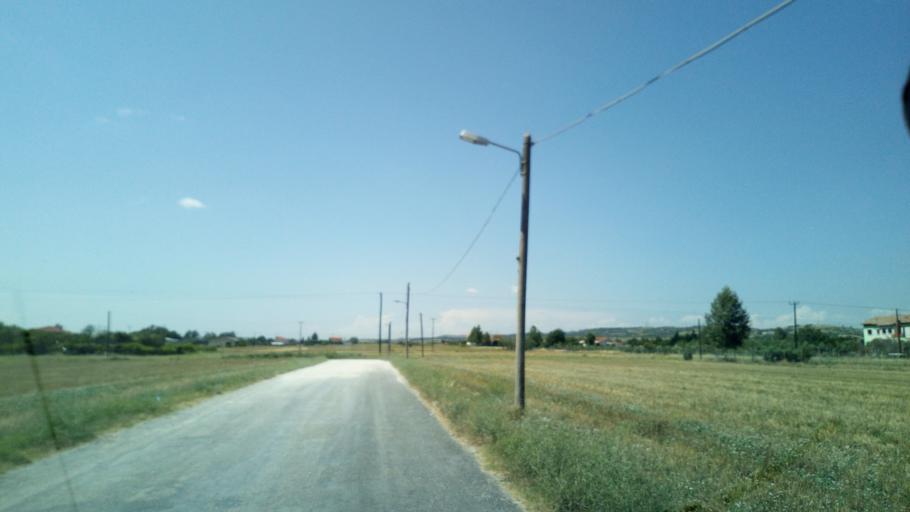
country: GR
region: Central Macedonia
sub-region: Nomos Thessalonikis
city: Lagkadas
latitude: 40.7673
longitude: 23.0863
